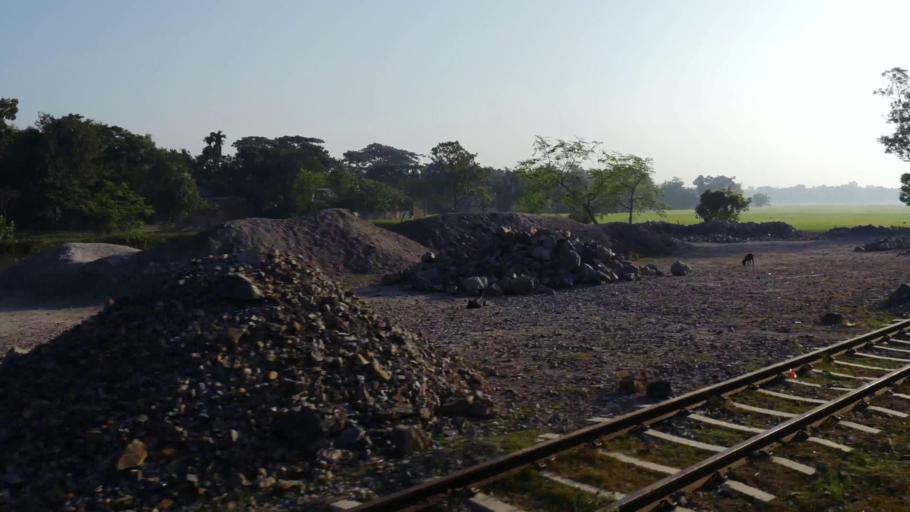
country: BD
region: Dhaka
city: Jamalpur
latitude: 24.9156
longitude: 89.9529
